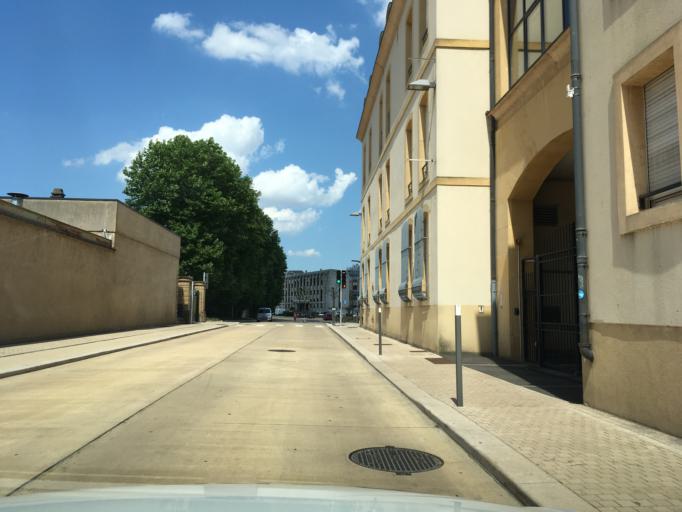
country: FR
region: Lorraine
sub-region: Departement de la Moselle
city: Metz
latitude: 49.1249
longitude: 6.1734
